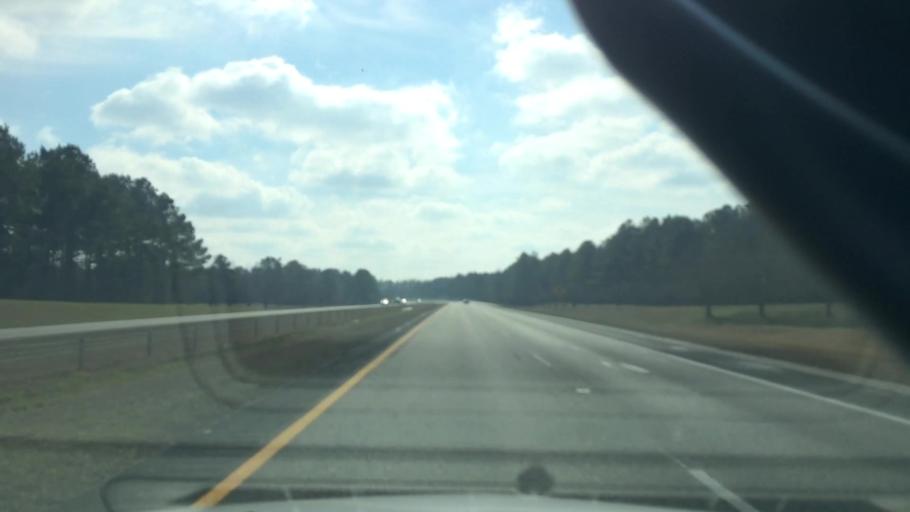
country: US
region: North Carolina
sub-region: Duplin County
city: Wallace
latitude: 34.6867
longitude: -77.9469
